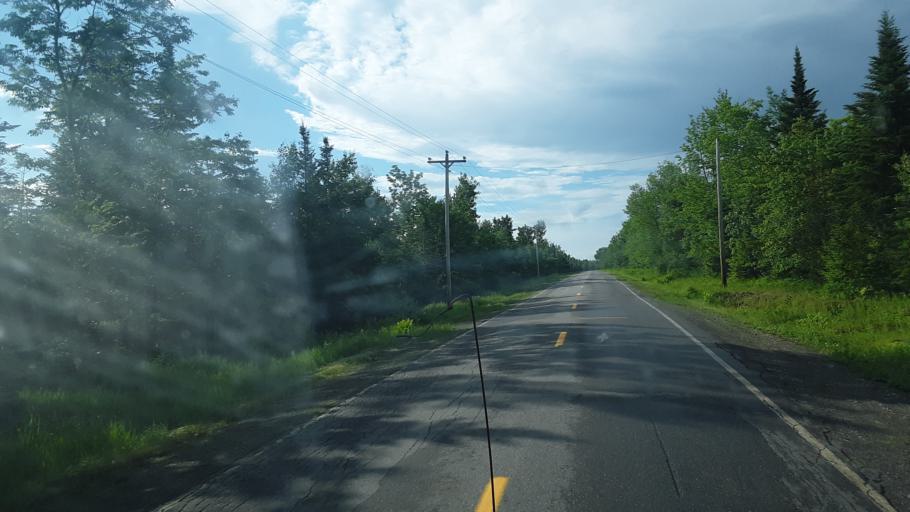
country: US
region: Maine
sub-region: Washington County
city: Calais
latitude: 45.1987
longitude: -67.5259
